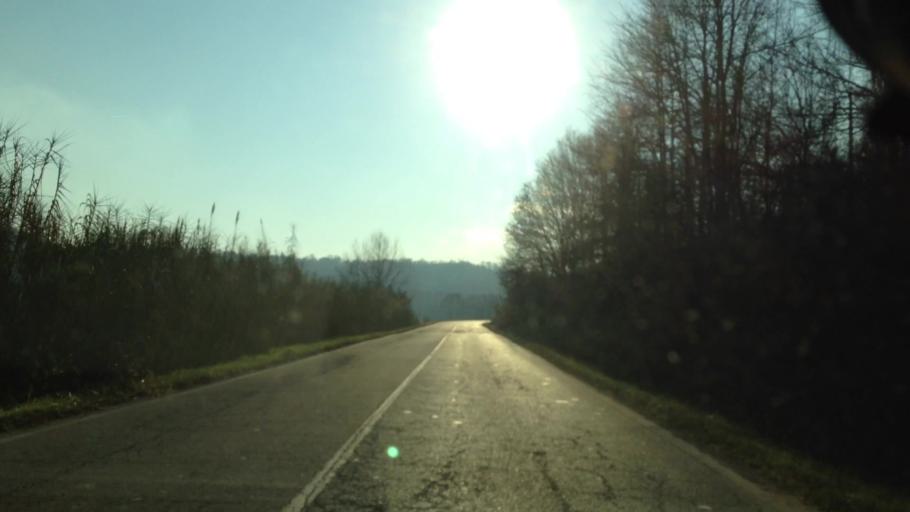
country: IT
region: Piedmont
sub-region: Provincia di Alessandria
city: Masio
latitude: 44.8428
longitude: 8.3919
